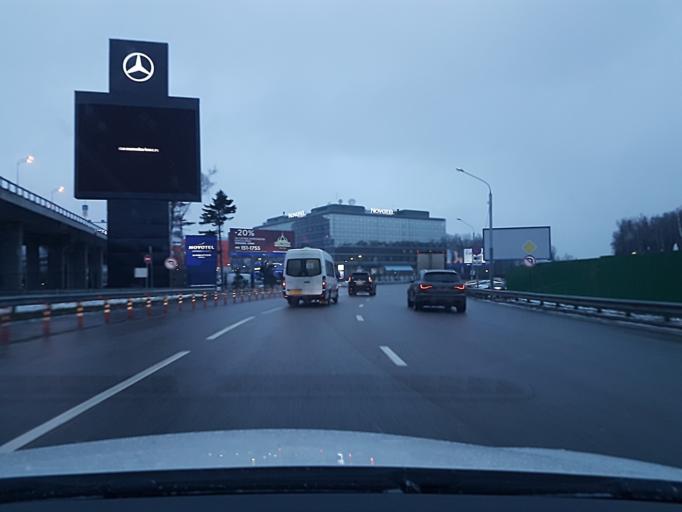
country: RU
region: Moscow
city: Khimki
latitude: 55.9603
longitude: 37.4147
